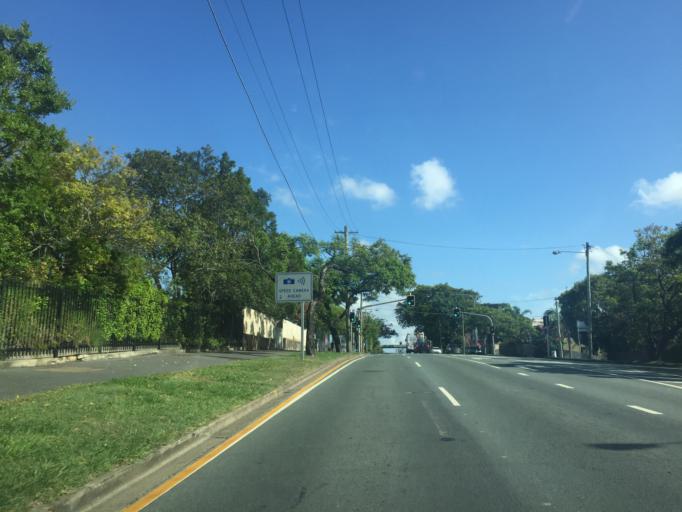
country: AU
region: Queensland
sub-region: Brisbane
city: Woolloongabba
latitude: -27.4781
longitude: 153.0356
